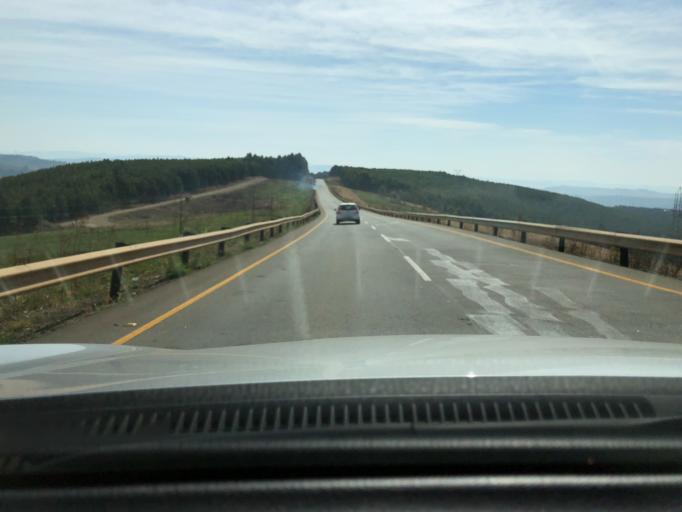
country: ZA
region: KwaZulu-Natal
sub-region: Sisonke District Municipality
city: Ixopo
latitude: -30.1121
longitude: 30.1201
